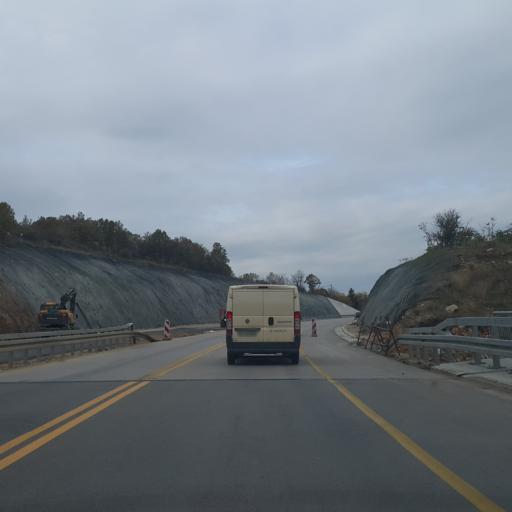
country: RS
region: Central Serbia
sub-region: Pirotski Okrug
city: Bela Palanka
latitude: 43.2194
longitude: 22.4114
